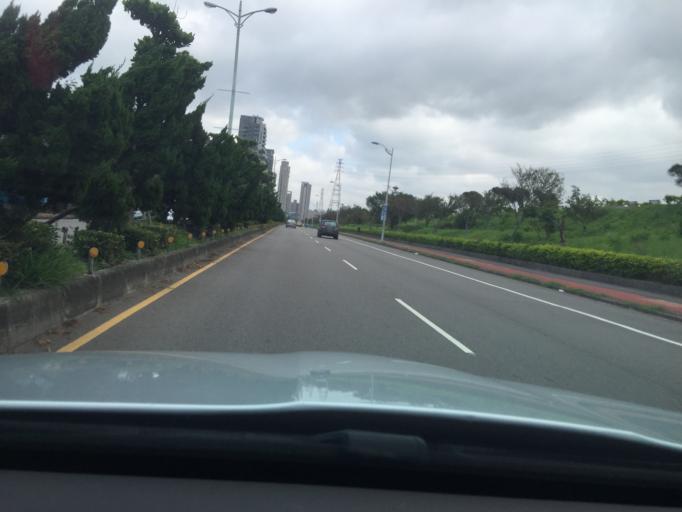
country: TW
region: Taiwan
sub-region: Hsinchu
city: Zhubei
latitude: 24.8229
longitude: 121.0028
